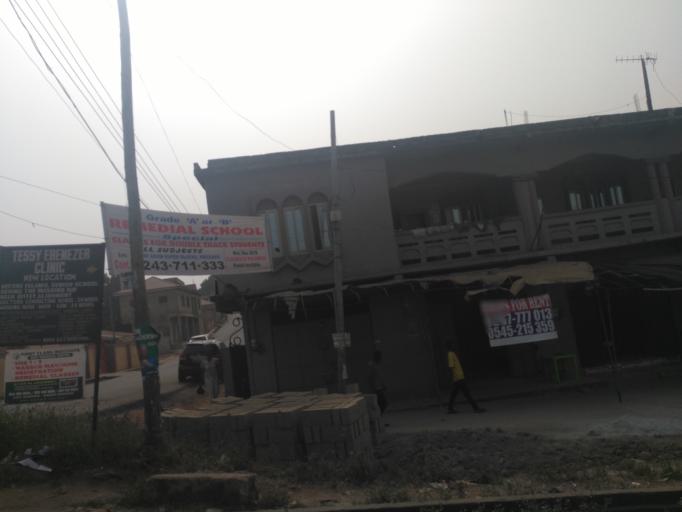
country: GH
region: Ashanti
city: Kumasi
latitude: 6.7101
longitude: -1.6382
